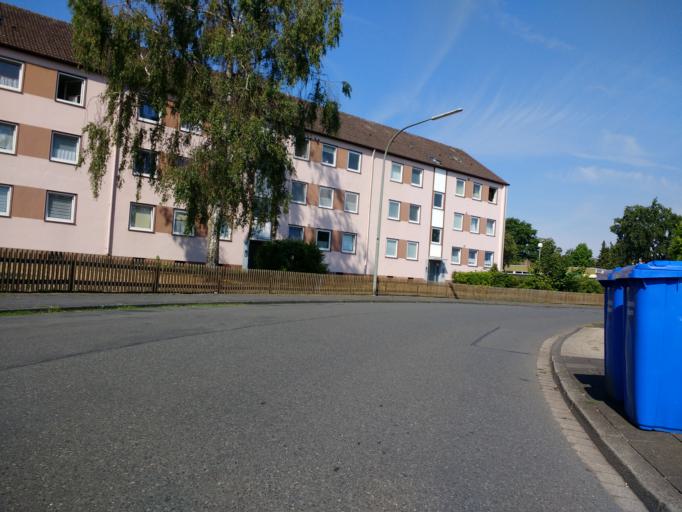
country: DE
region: Lower Saxony
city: Gifhorn
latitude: 52.4722
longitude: 10.5572
